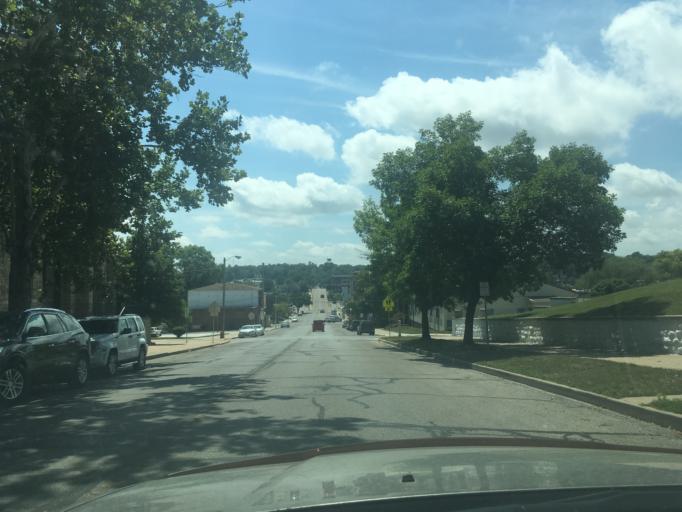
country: US
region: Kansas
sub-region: Atchison County
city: Atchison
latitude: 39.5646
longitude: -95.1191
